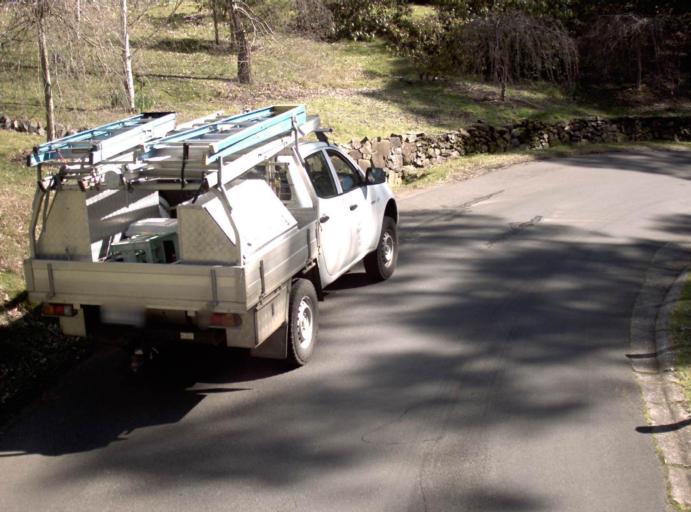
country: AU
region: Tasmania
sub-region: Launceston
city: East Launceston
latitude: -41.4557
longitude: 147.1651
